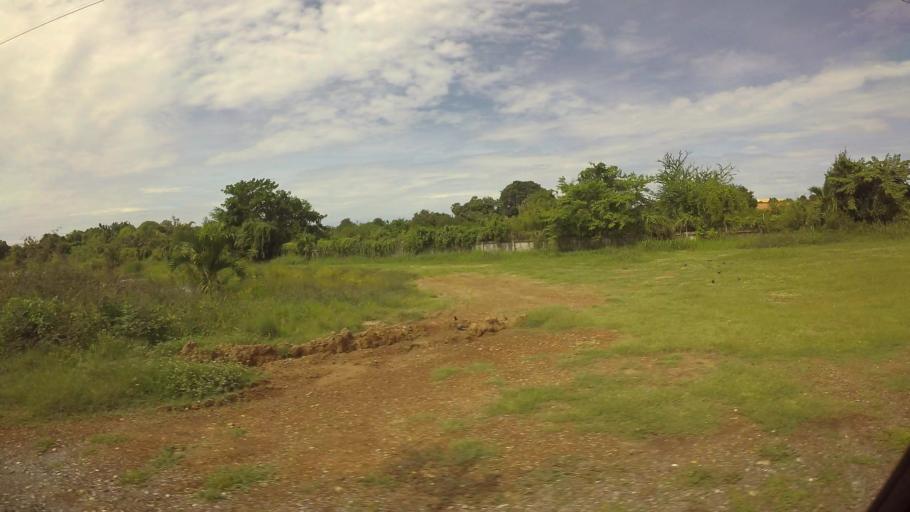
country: TH
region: Chon Buri
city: Sattahip
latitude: 12.6682
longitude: 100.9075
